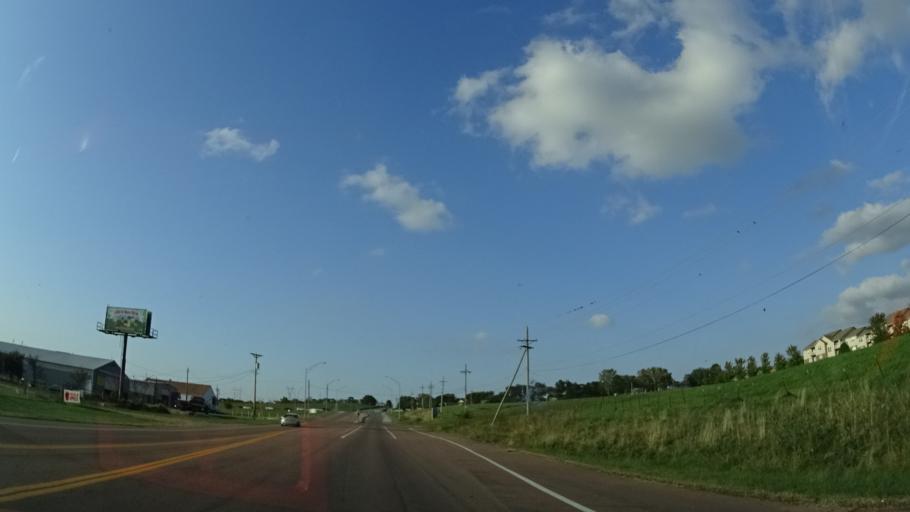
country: US
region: Nebraska
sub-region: Sarpy County
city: Offutt Air Force Base
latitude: 41.1589
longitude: -95.9667
